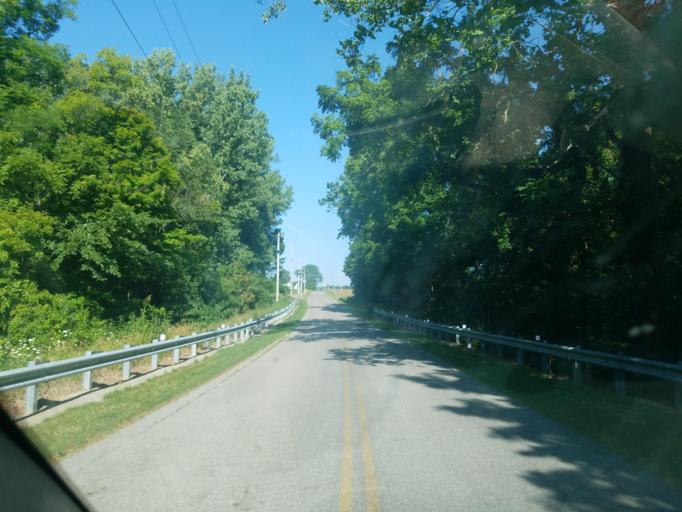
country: US
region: Ohio
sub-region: Logan County
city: Northwood
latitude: 40.4405
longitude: -83.6785
